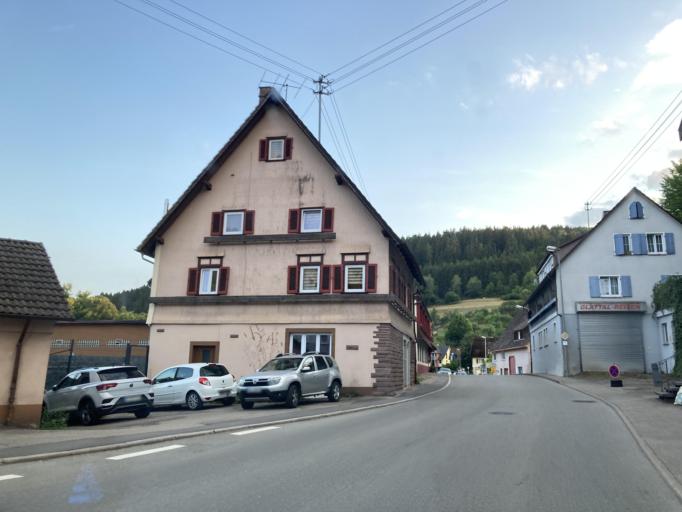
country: DE
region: Baden-Wuerttemberg
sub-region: Karlsruhe Region
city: Glatten
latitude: 48.3937
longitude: 8.5418
